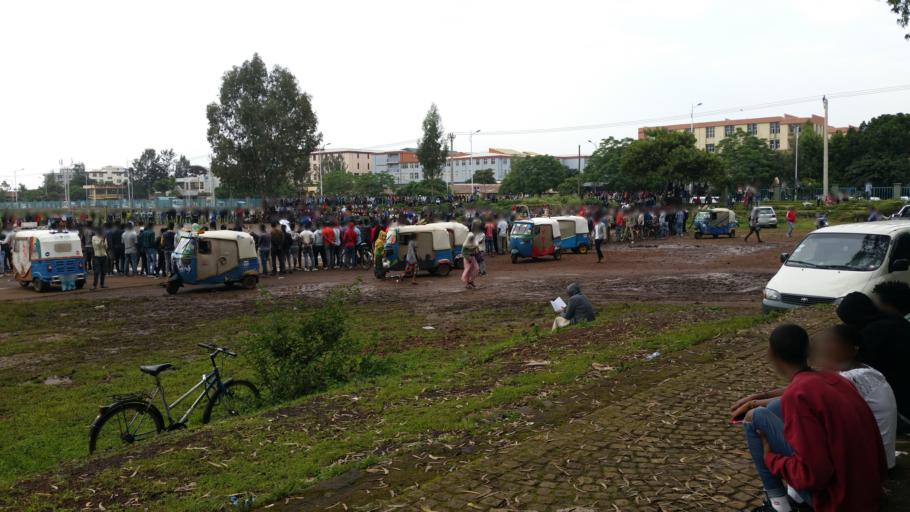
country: ET
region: Amhara
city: Bahir Dar
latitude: 11.5880
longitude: 37.3838
